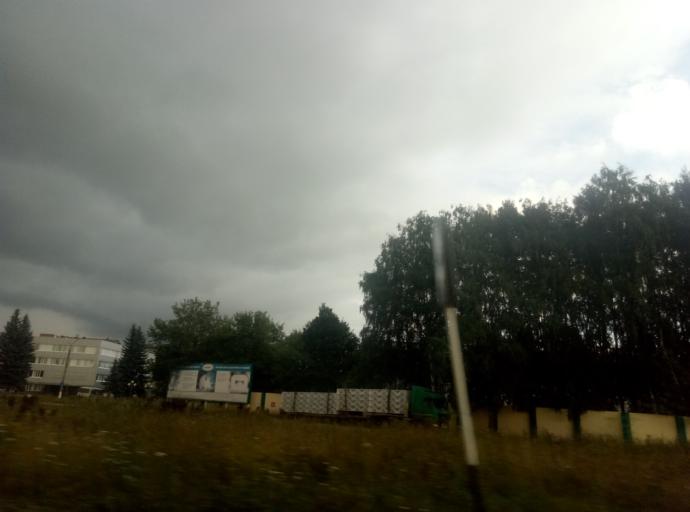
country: RU
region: Tula
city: Kireyevsk
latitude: 53.9567
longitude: 37.9384
